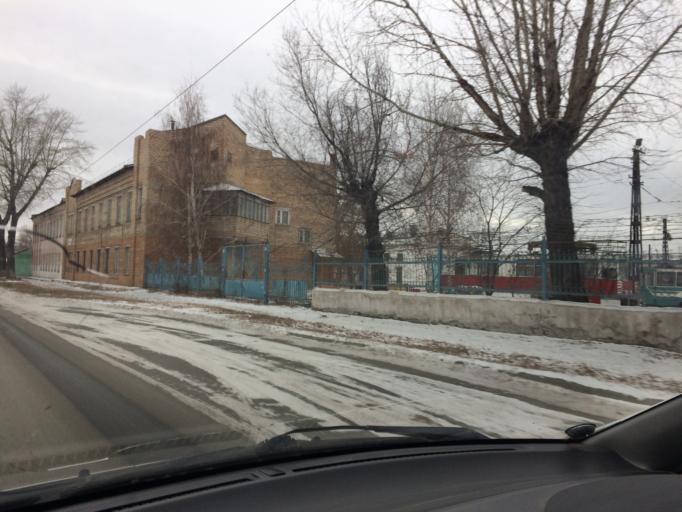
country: RU
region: Chelyabinsk
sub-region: Gorod Magnitogorsk
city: Magnitogorsk
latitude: 53.3862
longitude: 59.0763
